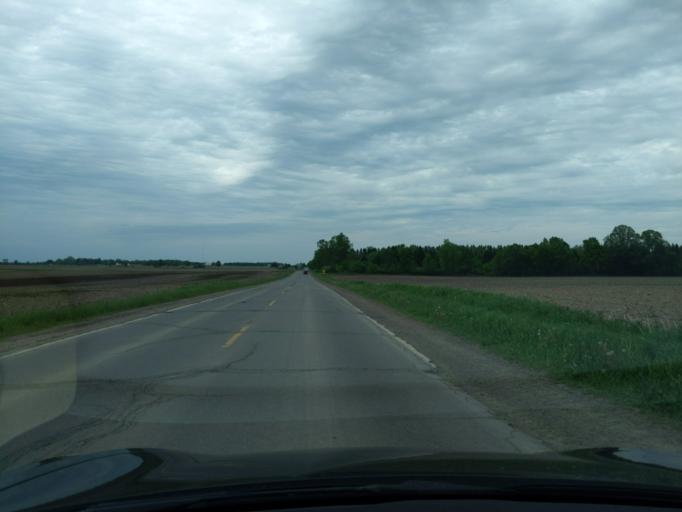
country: US
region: Michigan
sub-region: Ingham County
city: Williamston
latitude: 42.6362
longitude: -84.3639
